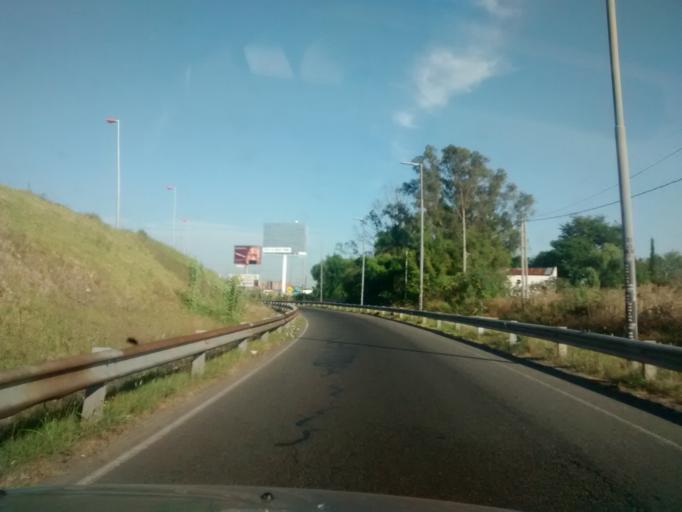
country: AR
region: Buenos Aires
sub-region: Partido de Avellaneda
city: Avellaneda
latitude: -34.6777
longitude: -58.3250
